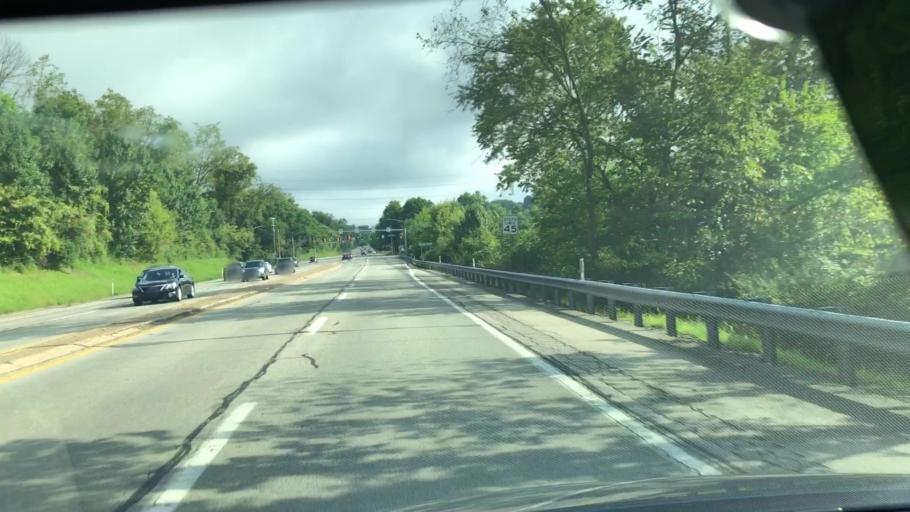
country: US
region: Pennsylvania
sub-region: Allegheny County
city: Bryn Mawr
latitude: 40.3117
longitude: -80.0905
